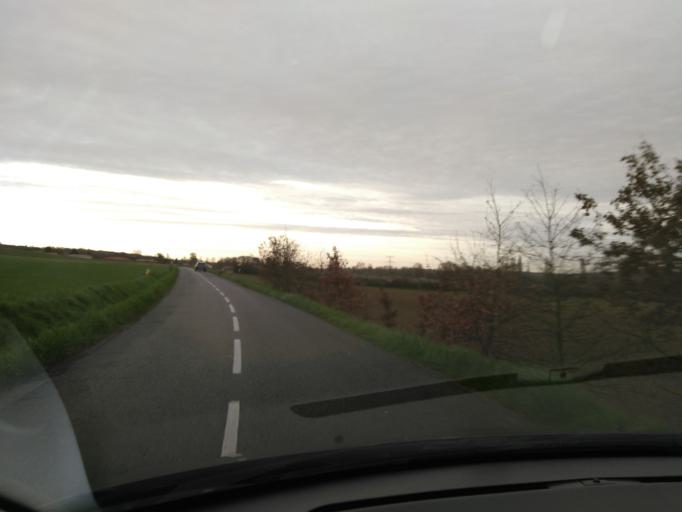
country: FR
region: Midi-Pyrenees
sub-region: Departement de la Haute-Garonne
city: Labastide-Saint-Sernin
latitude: 43.7437
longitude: 1.4824
